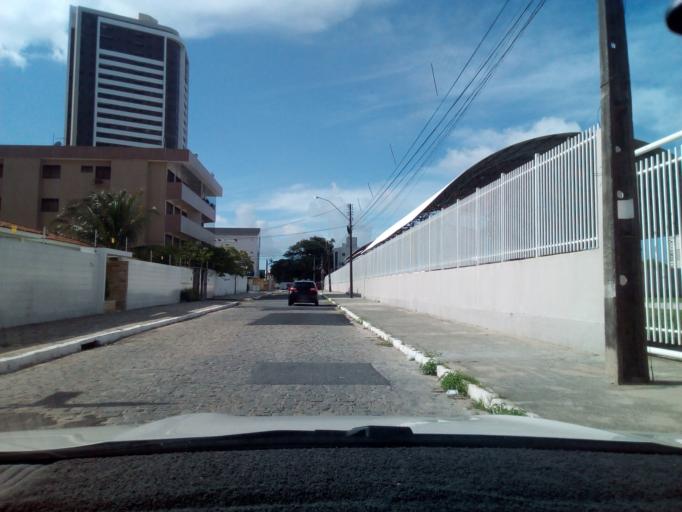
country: BR
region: Paraiba
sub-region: Joao Pessoa
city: Joao Pessoa
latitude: -7.1119
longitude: -34.8515
